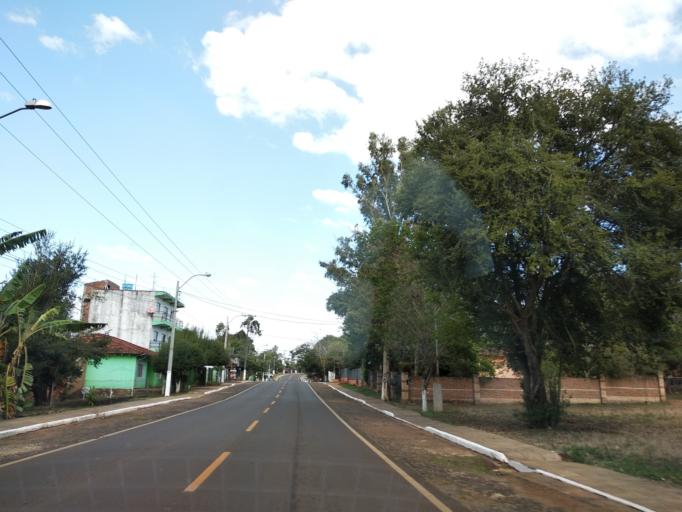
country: PY
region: Itapua
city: San Juan del Parana
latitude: -27.2996
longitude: -55.9649
